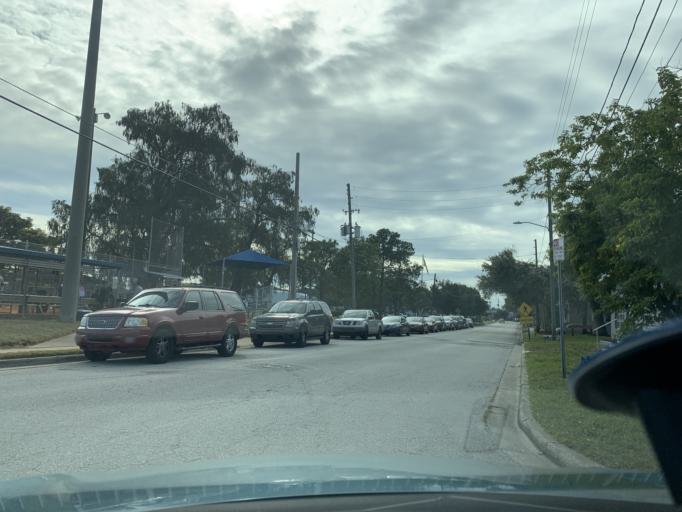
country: US
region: Florida
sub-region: Pinellas County
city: Saint Petersburg
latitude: 27.7869
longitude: -82.6591
